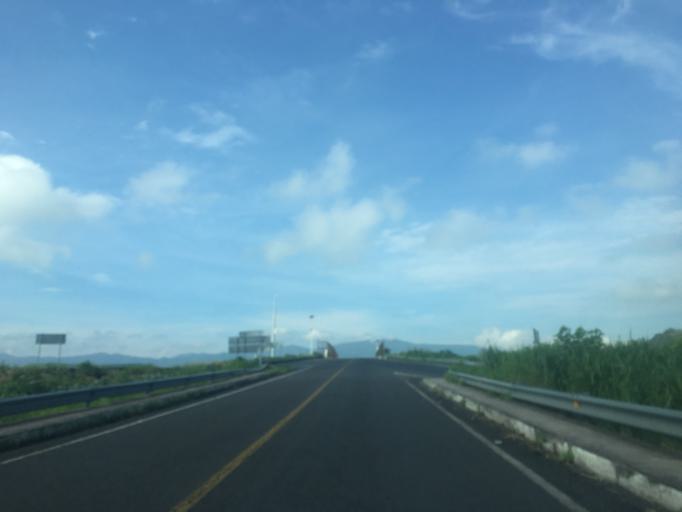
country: MX
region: Nayarit
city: Jala
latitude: 21.0914
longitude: -104.4382
